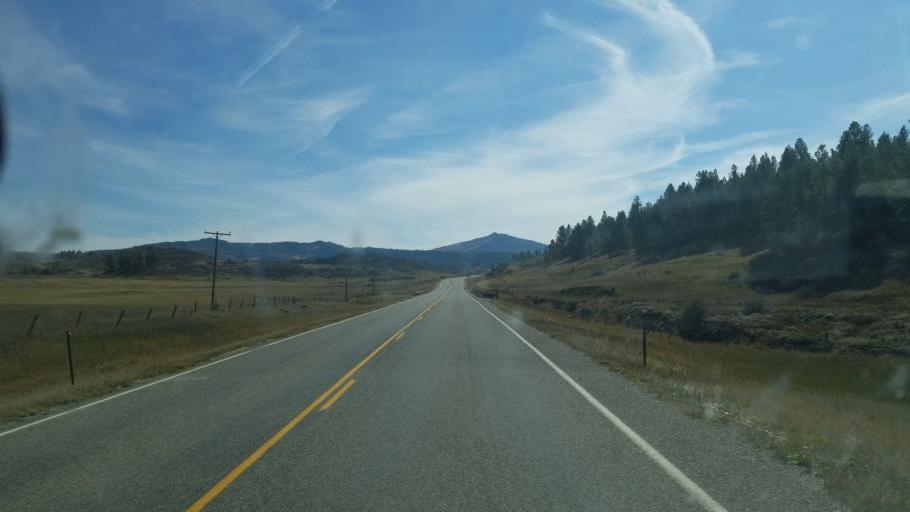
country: US
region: New Mexico
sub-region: Rio Arriba County
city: Dulce
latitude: 37.0177
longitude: -106.8114
